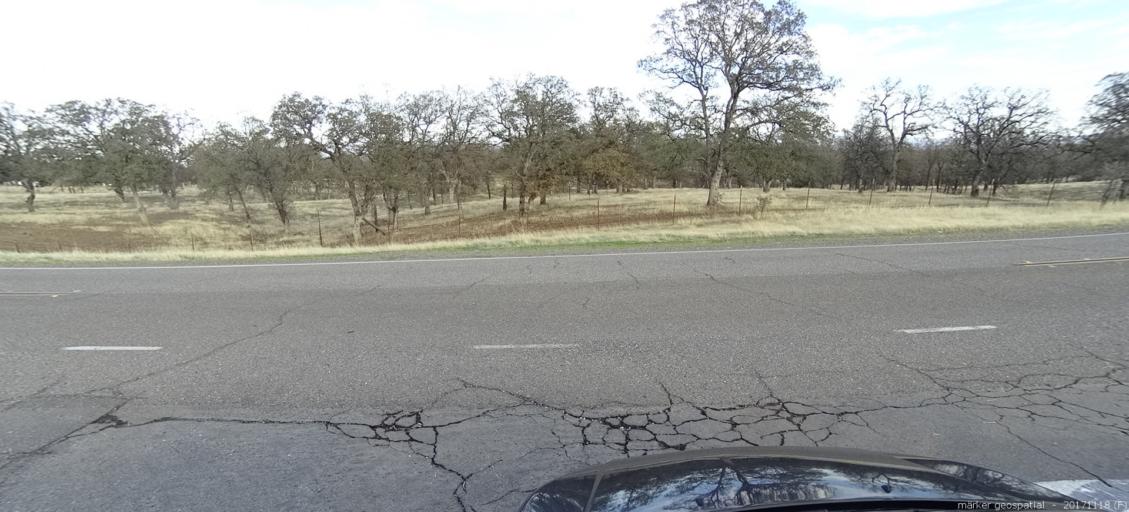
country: US
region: California
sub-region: Shasta County
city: Cottonwood
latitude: 40.4132
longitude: -122.2725
